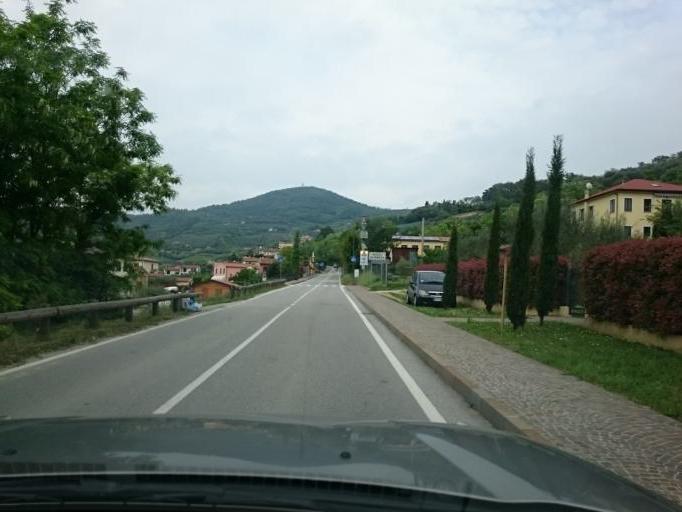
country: IT
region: Veneto
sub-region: Provincia di Padova
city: Arqua Petrarca
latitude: 45.2642
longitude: 11.7136
